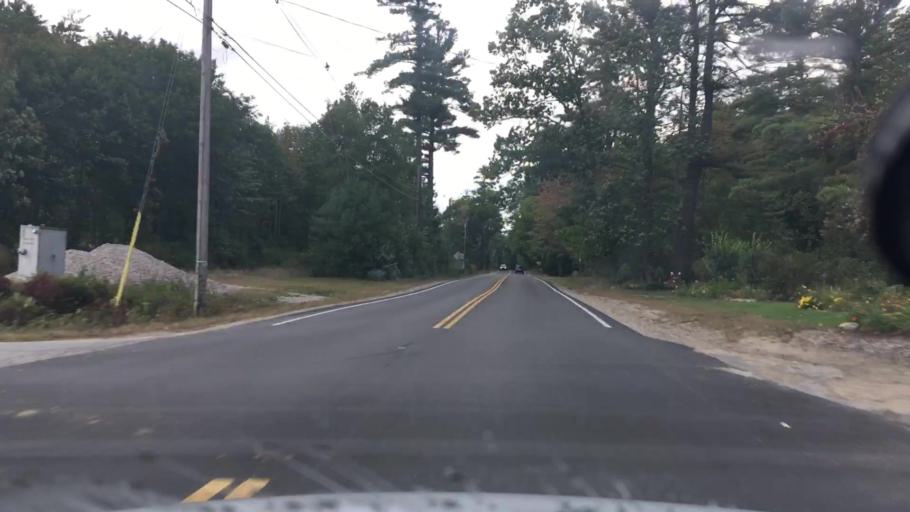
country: US
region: New Hampshire
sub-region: Carroll County
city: Sanbornville
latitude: 43.5446
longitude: -71.0273
